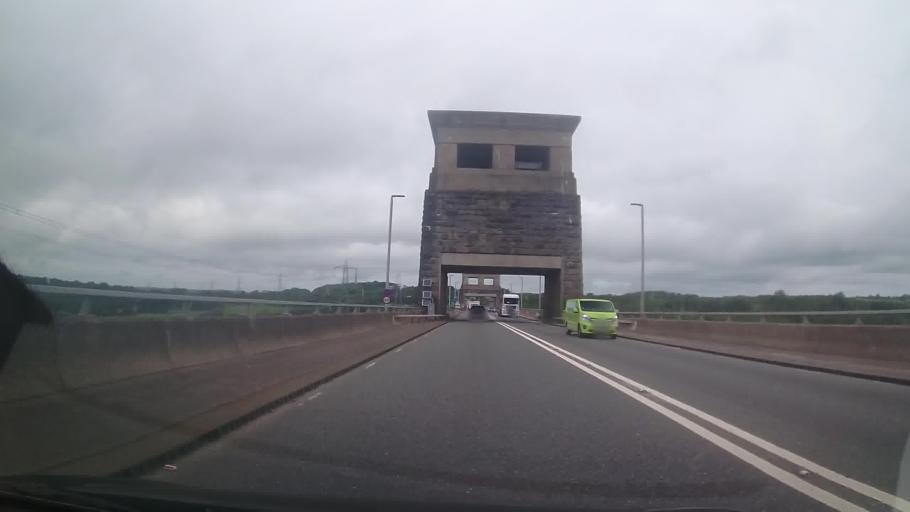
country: GB
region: Wales
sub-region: Anglesey
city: Llanfairpwllgwyngyll
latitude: 53.2161
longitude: -4.1858
